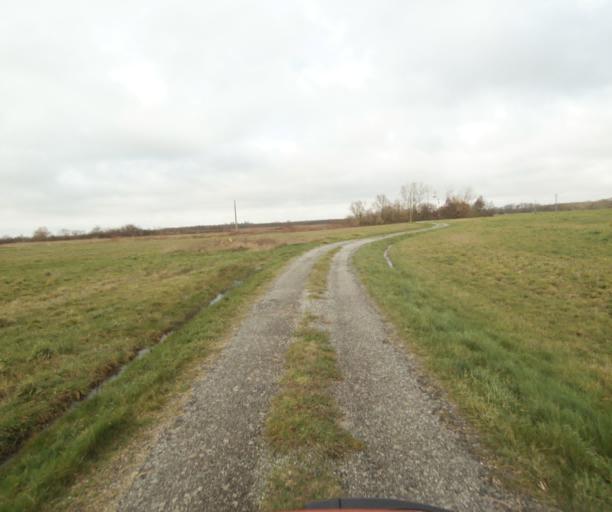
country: FR
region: Midi-Pyrenees
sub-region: Departement de l'Ariege
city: La Tour-du-Crieu
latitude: 43.1569
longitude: 1.6916
